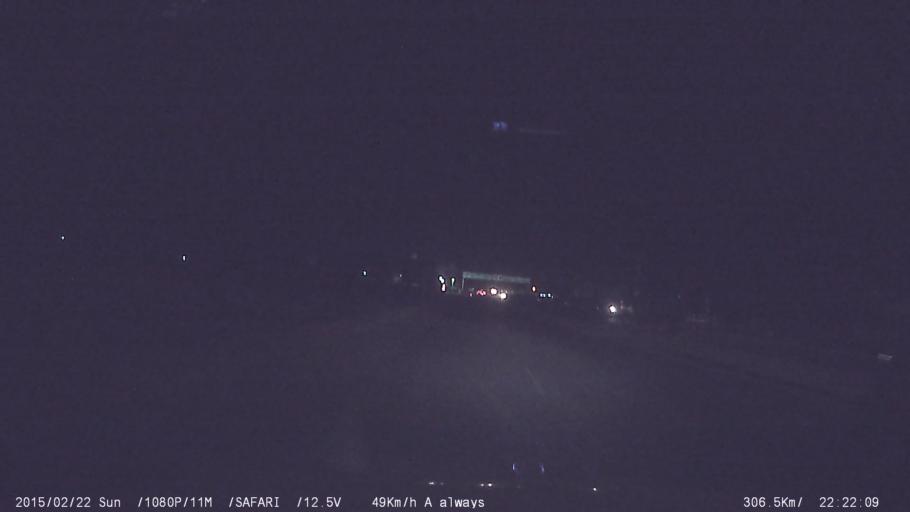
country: IN
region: Tamil Nadu
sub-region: Karur
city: Karur
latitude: 11.0115
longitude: 78.0686
